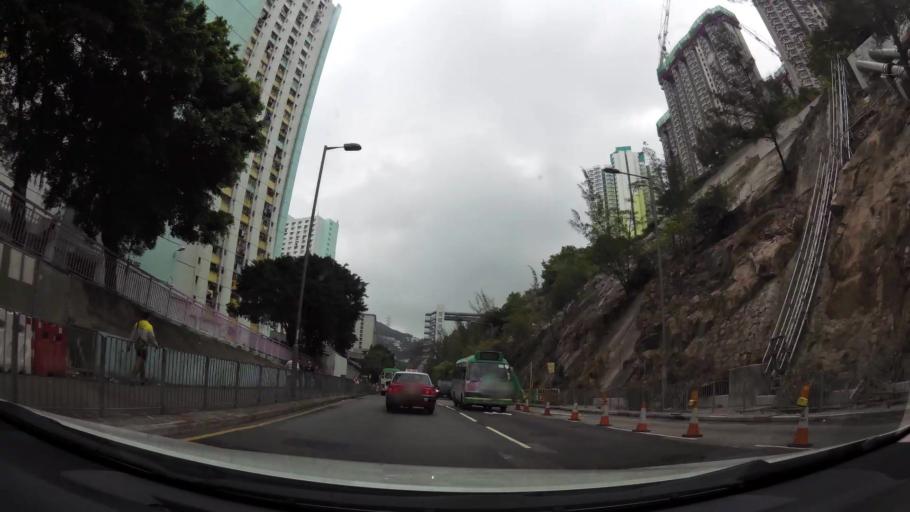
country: HK
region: Kowloon City
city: Kowloon
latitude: 22.3272
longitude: 114.2267
